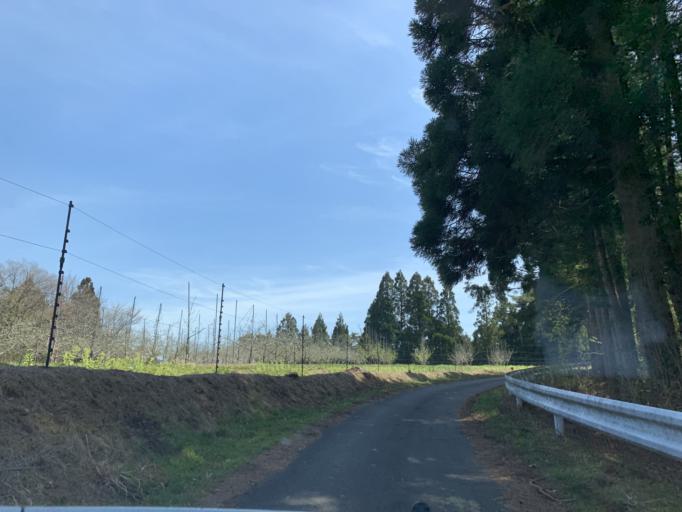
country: JP
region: Iwate
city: Ichinoseki
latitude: 38.8360
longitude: 141.2883
